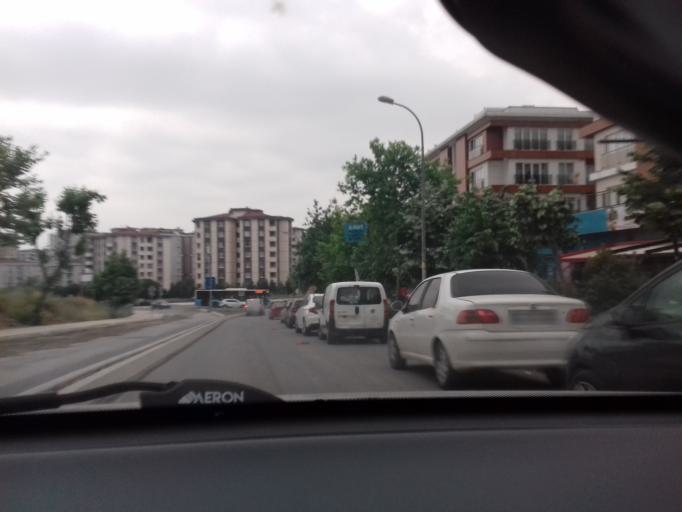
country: TR
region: Istanbul
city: Sultanbeyli
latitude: 40.9315
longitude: 29.2964
